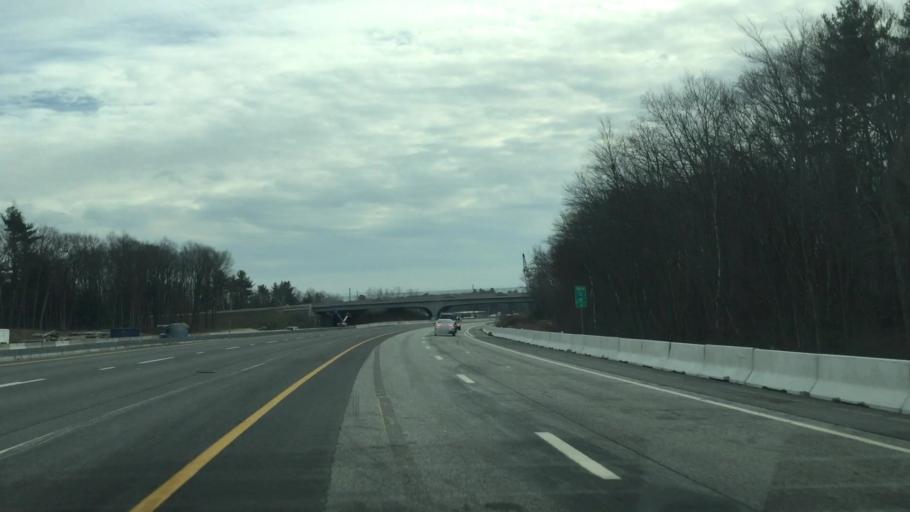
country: US
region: New Hampshire
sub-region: Rockingham County
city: Derry
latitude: 42.8832
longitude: -71.3469
